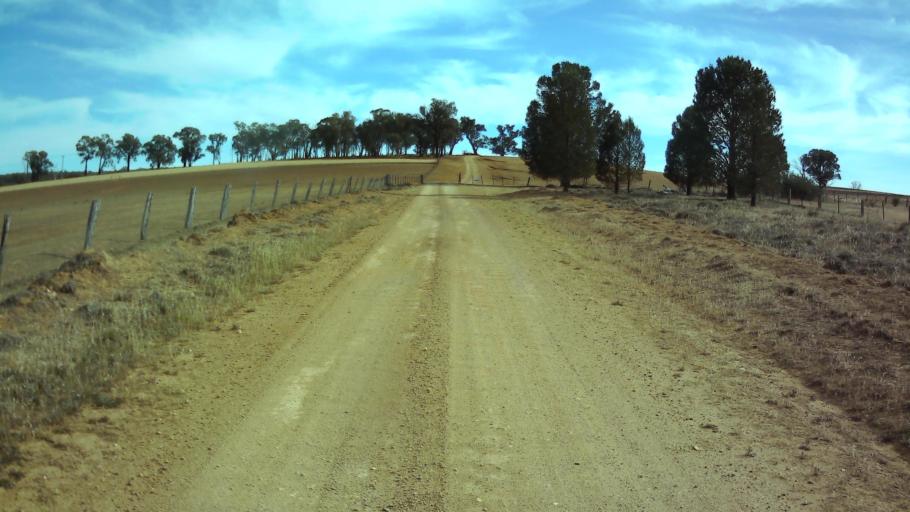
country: AU
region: New South Wales
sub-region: Weddin
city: Grenfell
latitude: -33.8970
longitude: 148.2037
